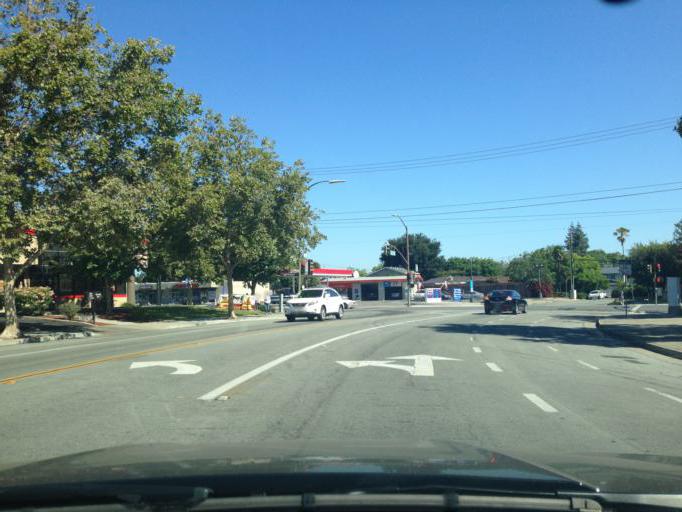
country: US
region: California
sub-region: Santa Clara County
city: Cupertino
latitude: 37.3090
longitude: -121.9932
